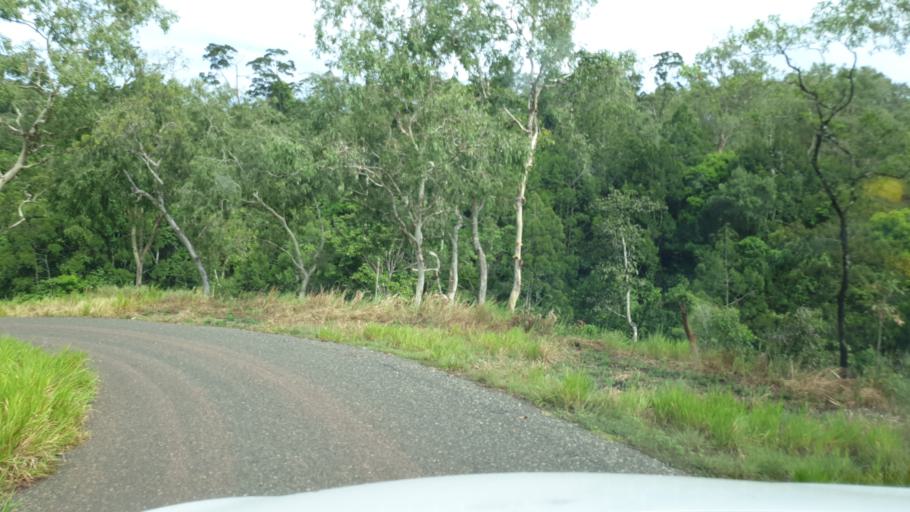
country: PG
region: National Capital
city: Port Moresby
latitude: -9.4352
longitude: 147.3955
